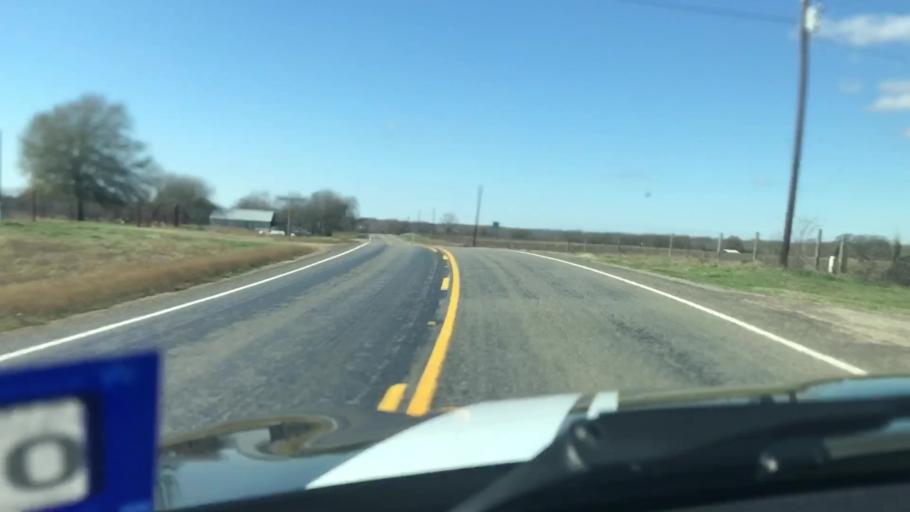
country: US
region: Texas
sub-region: Robertson County
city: Calvert
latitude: 30.8846
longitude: -96.7523
